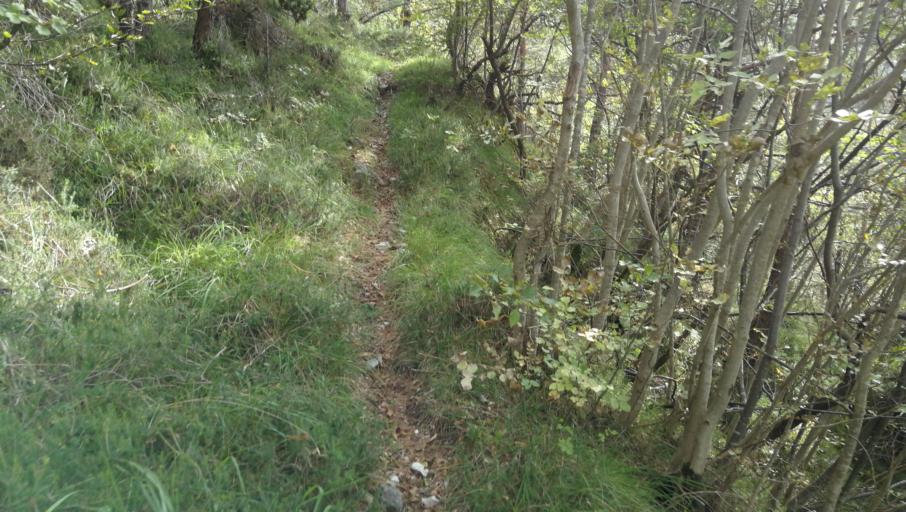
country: IT
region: Trentino-Alto Adige
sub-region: Provincia di Trento
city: Condino
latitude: 45.8849
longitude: 10.6049
